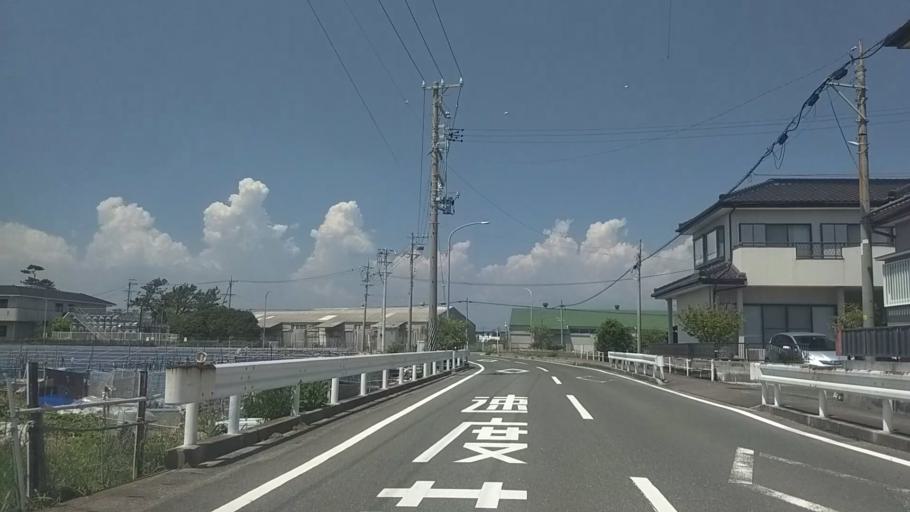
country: JP
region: Shizuoka
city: Kosai-shi
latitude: 34.6849
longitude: 137.5779
